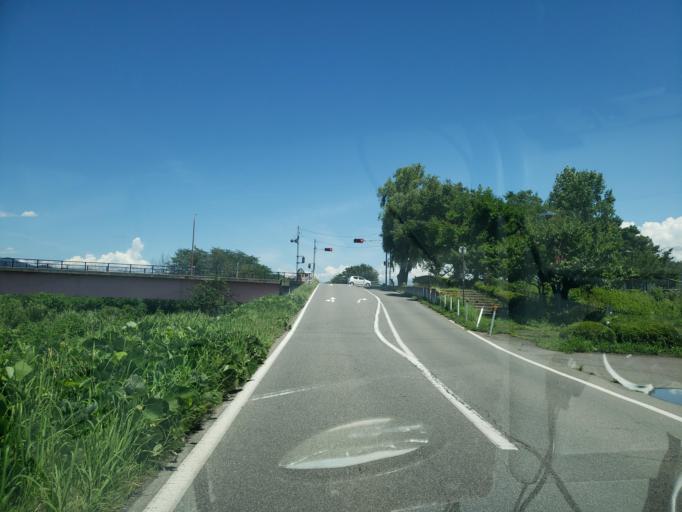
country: JP
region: Nagano
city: Nagano-shi
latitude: 36.5383
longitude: 138.1168
